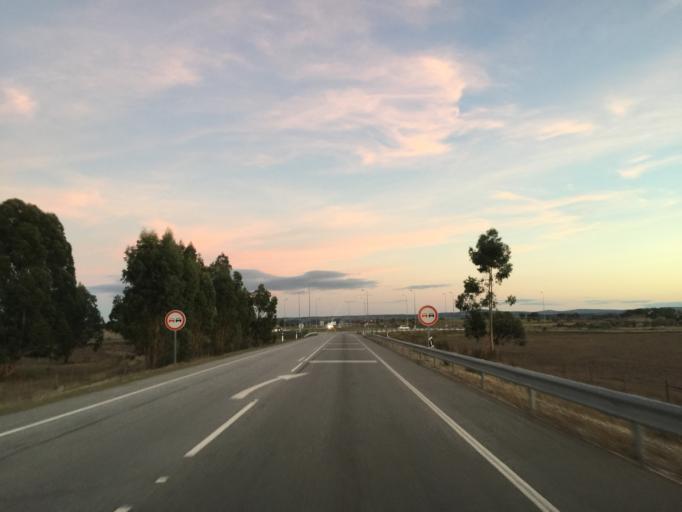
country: PT
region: Portalegre
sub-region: Alter do Chao
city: Alter do Chao
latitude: 39.2976
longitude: -7.6320
